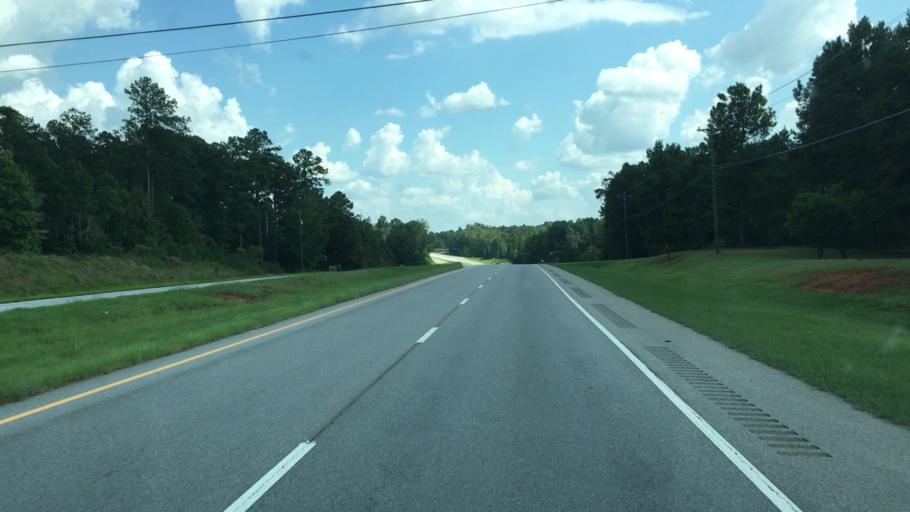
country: US
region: Georgia
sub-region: Putnam County
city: Eatonton
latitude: 33.2455
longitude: -83.3246
